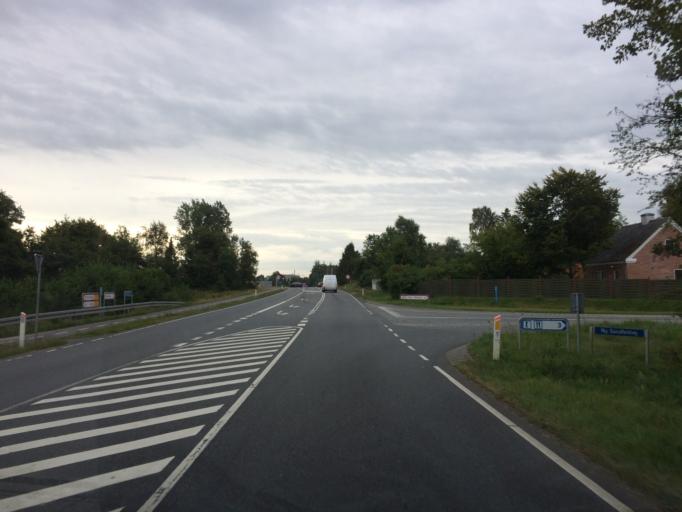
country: DK
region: Central Jutland
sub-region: Ikast-Brande Kommune
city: Brande
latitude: 55.9580
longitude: 9.1068
